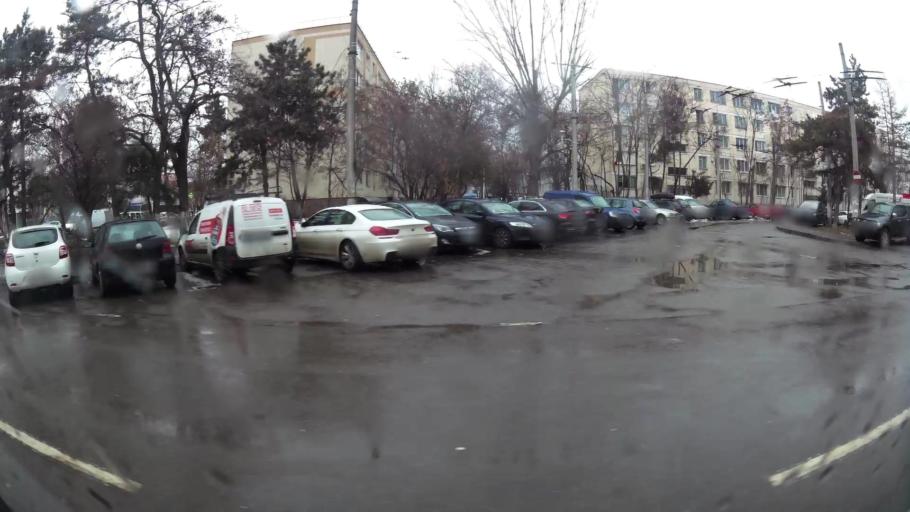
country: RO
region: Ilfov
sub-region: Comuna Chiajna
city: Rosu
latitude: 44.4158
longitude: 26.0146
